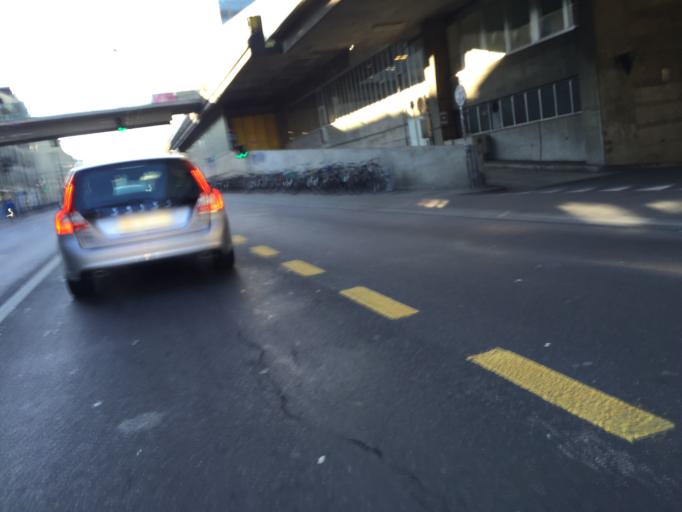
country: CH
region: Bern
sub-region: Bern-Mittelland District
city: Bern
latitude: 46.9504
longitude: 7.4406
